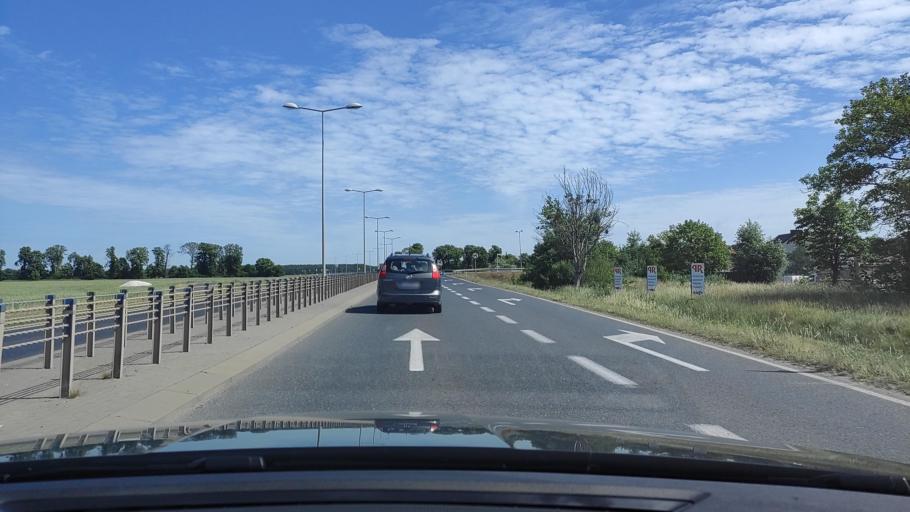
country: PL
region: Greater Poland Voivodeship
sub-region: Powiat poznanski
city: Murowana Goslina
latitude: 52.5461
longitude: 16.9893
